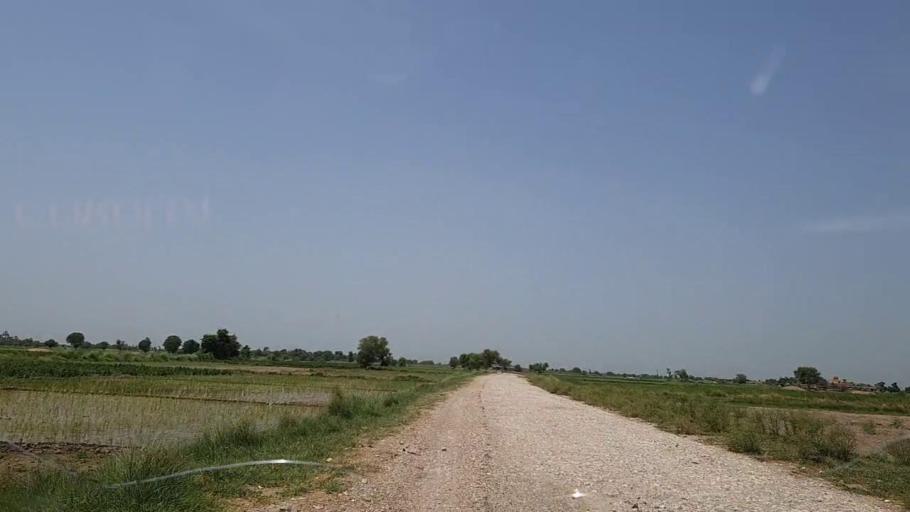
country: PK
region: Sindh
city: Tharu Shah
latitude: 26.9187
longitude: 68.0590
